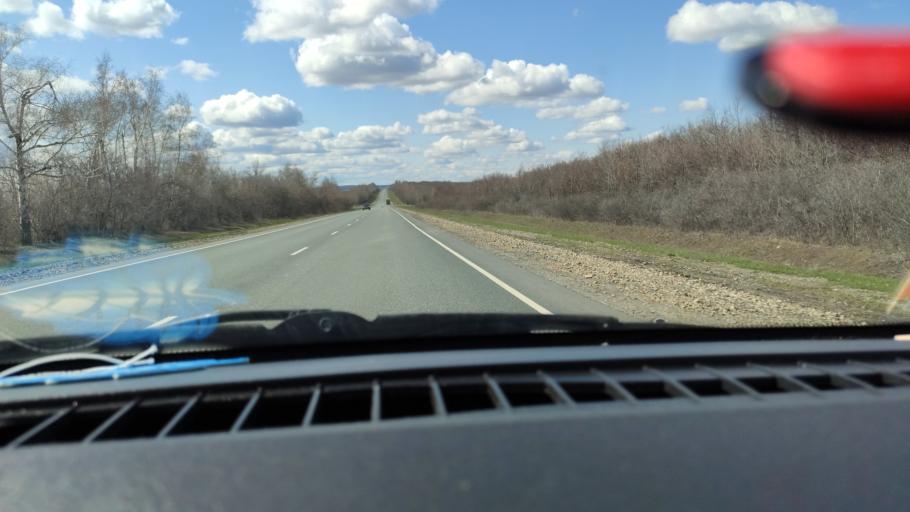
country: RU
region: Saratov
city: Khvalynsk
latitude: 52.6074
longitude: 48.1538
